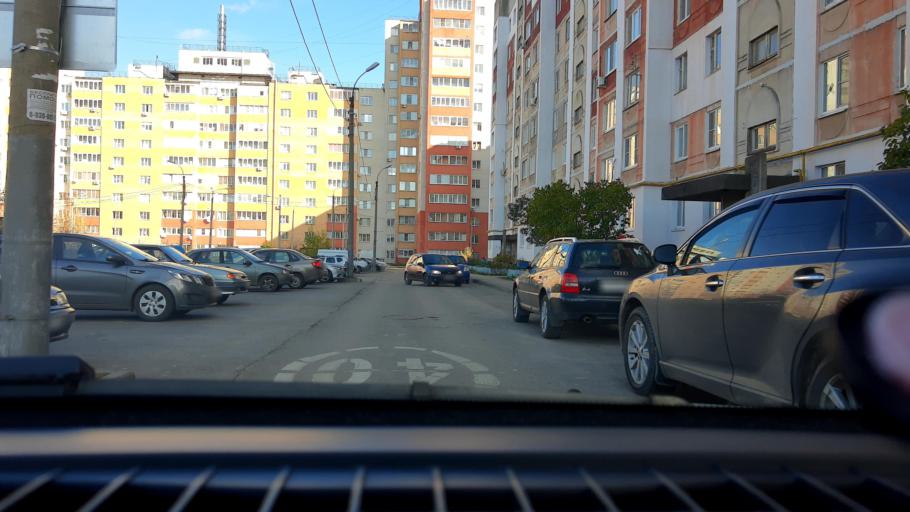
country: RU
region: Nizjnij Novgorod
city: Kstovo
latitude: 56.1587
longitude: 44.2146
